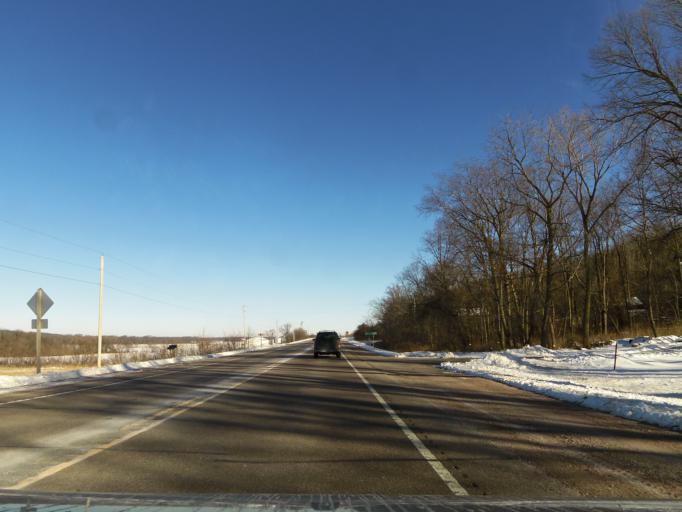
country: US
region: Wisconsin
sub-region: Columbia County
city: Lake Wisconsin
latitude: 43.5056
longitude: -89.6014
